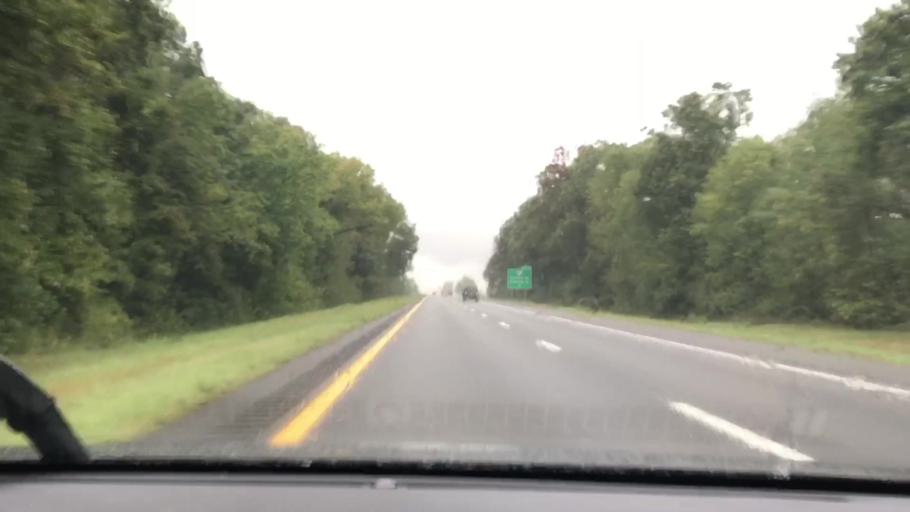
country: US
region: Tennessee
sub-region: Montgomery County
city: Clarksville
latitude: 36.5625
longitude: -87.2534
